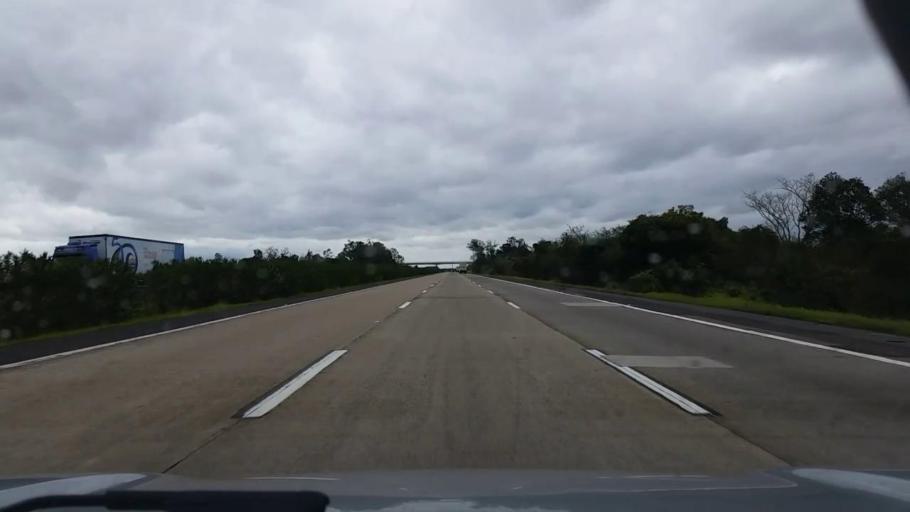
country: BR
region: Rio Grande do Sul
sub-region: Rolante
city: Rolante
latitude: -29.8863
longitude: -50.6492
